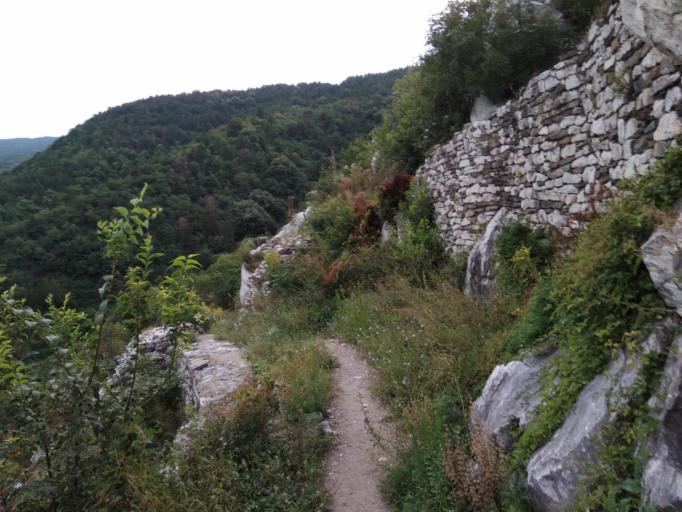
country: BG
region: Plovdiv
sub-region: Obshtina Asenovgrad
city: Asenovgrad
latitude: 41.9865
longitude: 24.8735
